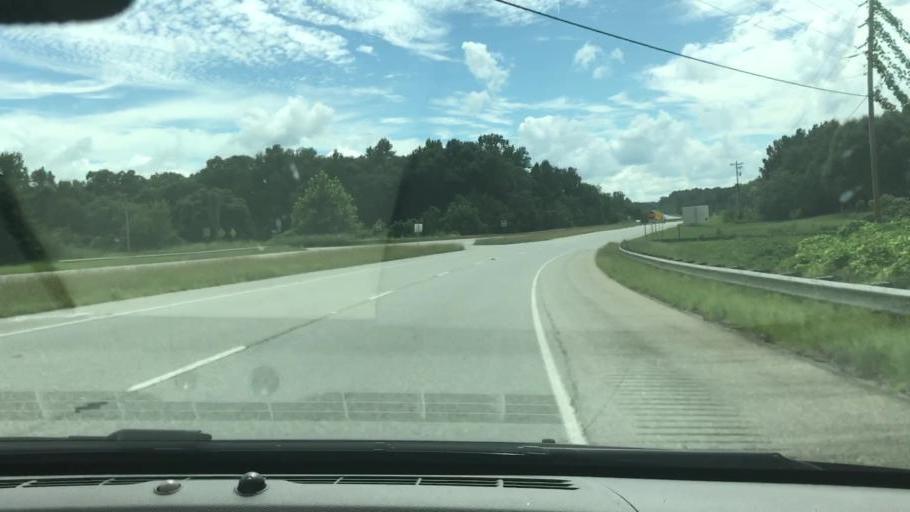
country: US
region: Georgia
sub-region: Stewart County
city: Lumpkin
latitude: 32.1574
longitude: -84.8287
